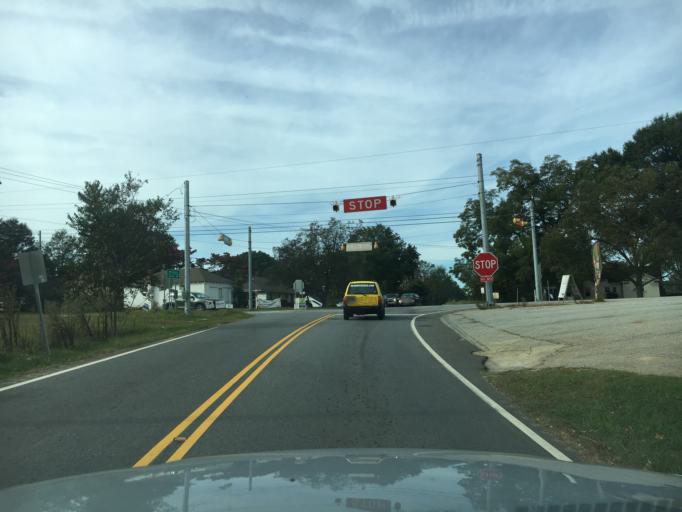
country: US
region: South Carolina
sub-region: Spartanburg County
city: Duncan
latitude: 34.8910
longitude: -82.1403
